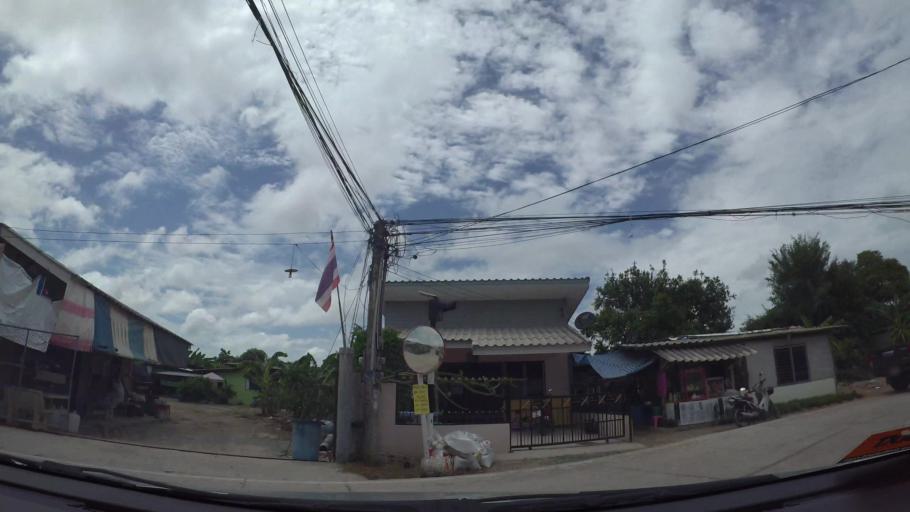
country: TH
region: Chon Buri
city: Sattahip
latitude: 12.6781
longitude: 100.9005
